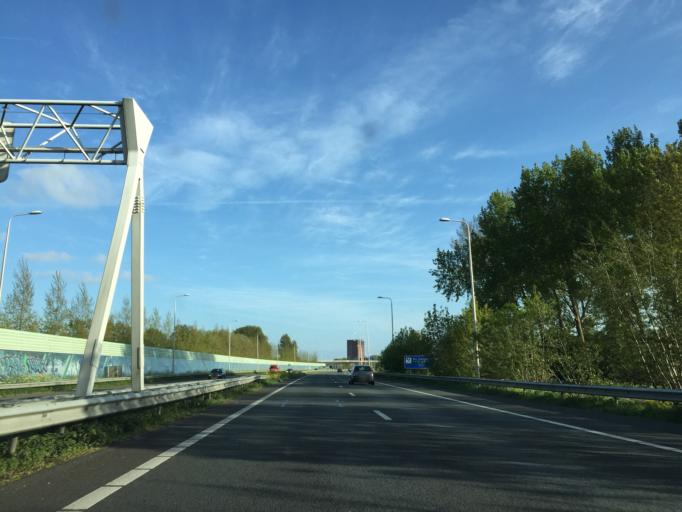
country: NL
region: North Holland
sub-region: Gemeente Hoorn
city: Hoorn
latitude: 52.6600
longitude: 5.0370
